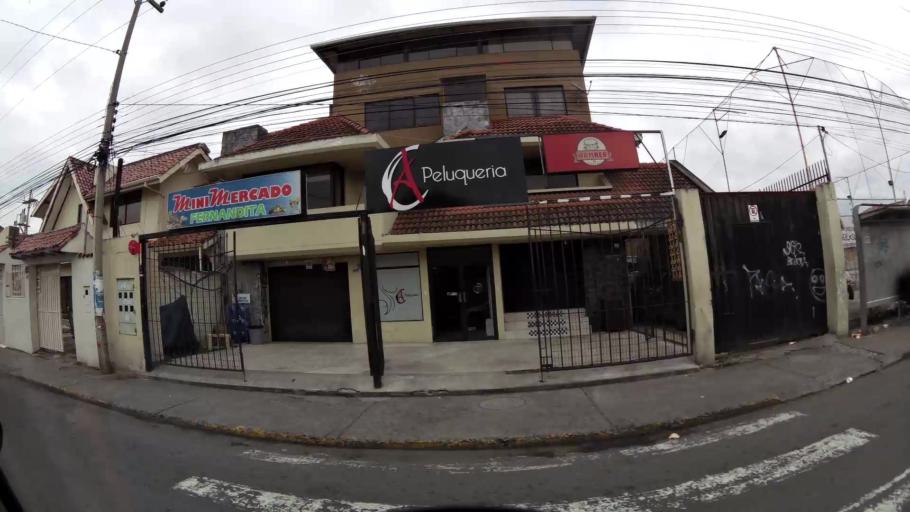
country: EC
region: Azuay
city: Cuenca
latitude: -2.9051
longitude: -79.0154
